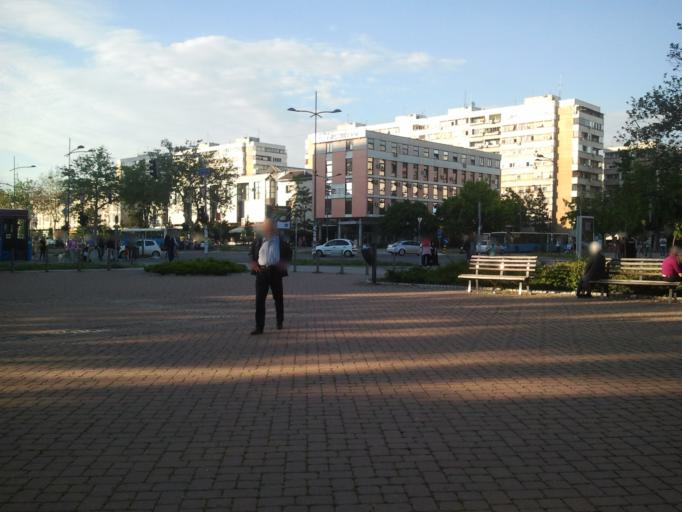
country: RS
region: Autonomna Pokrajina Vojvodina
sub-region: Juznobacki Okrug
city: Novi Sad
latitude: 45.2411
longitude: 19.8425
